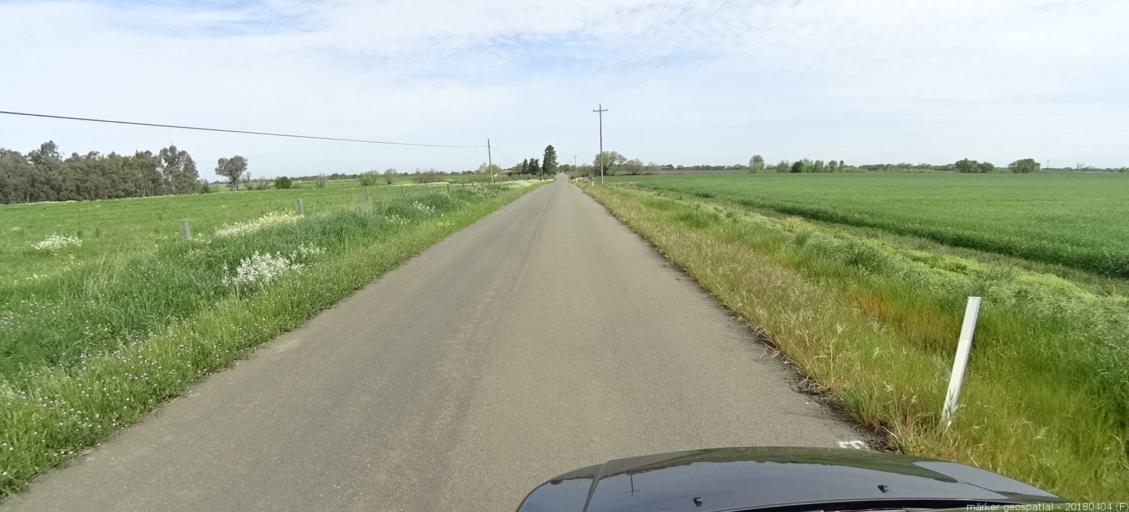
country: US
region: California
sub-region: Sacramento County
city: Herald
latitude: 38.3020
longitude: -121.2772
